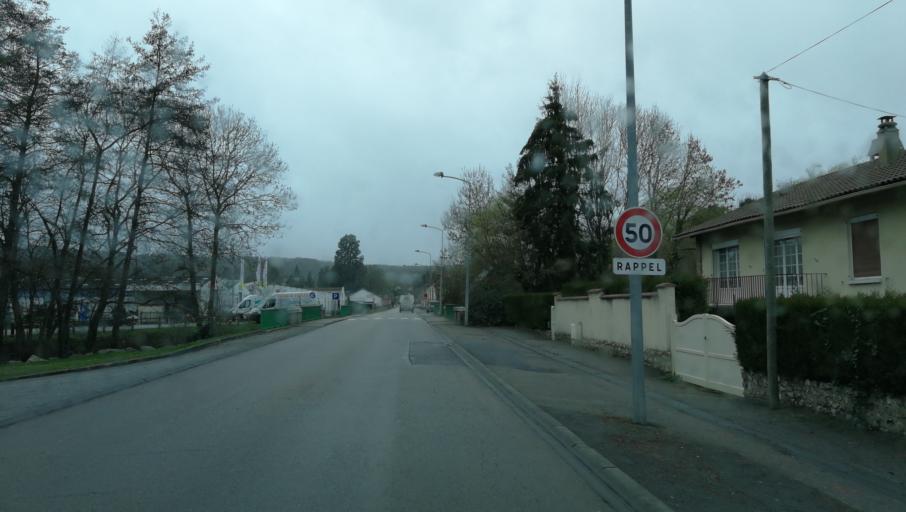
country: FR
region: Haute-Normandie
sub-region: Departement de l'Eure
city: Brionne
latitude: 49.1929
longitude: 0.7191
